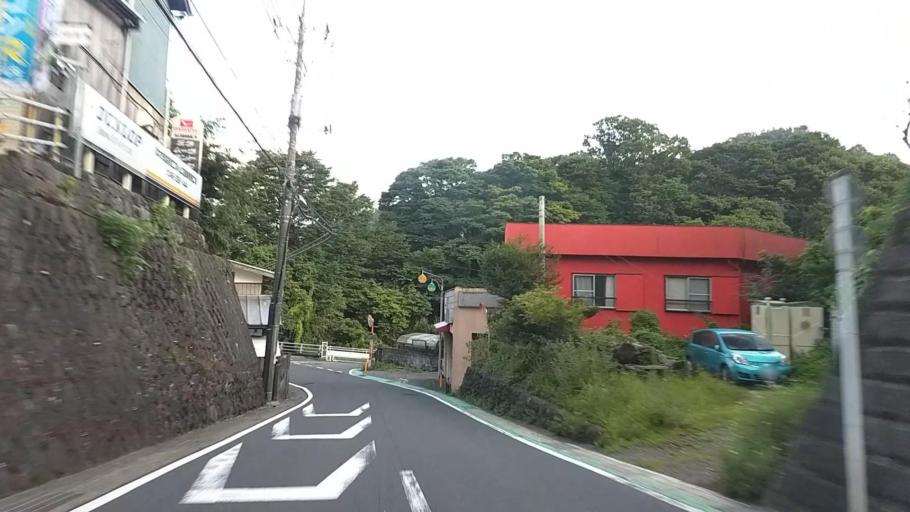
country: JP
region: Kanagawa
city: Atsugi
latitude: 35.4848
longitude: 139.2734
